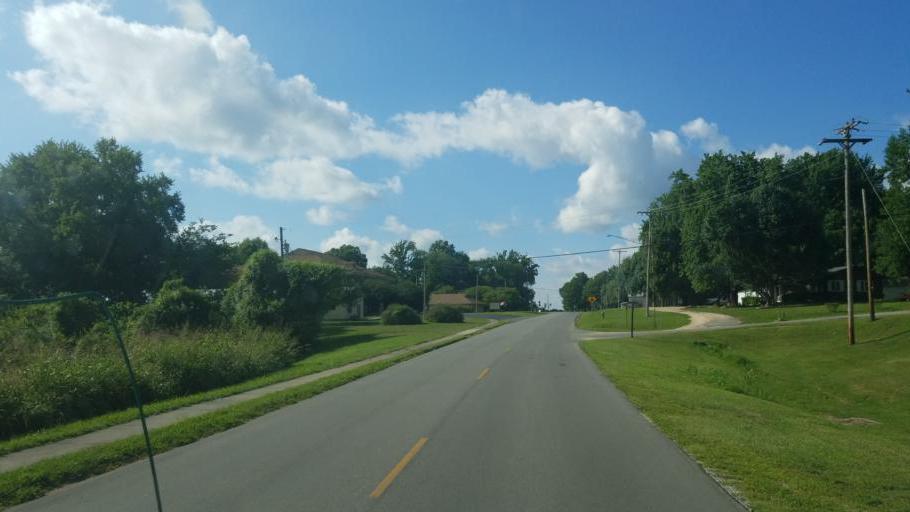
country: US
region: Illinois
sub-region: Union County
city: Cobden
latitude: 37.5744
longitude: -89.3203
